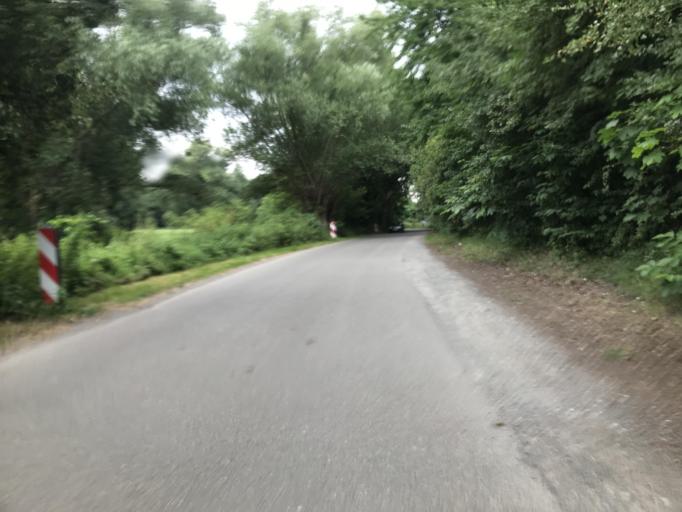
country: DE
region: Saxony-Anhalt
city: Quedlinburg
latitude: 51.8027
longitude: 11.1659
